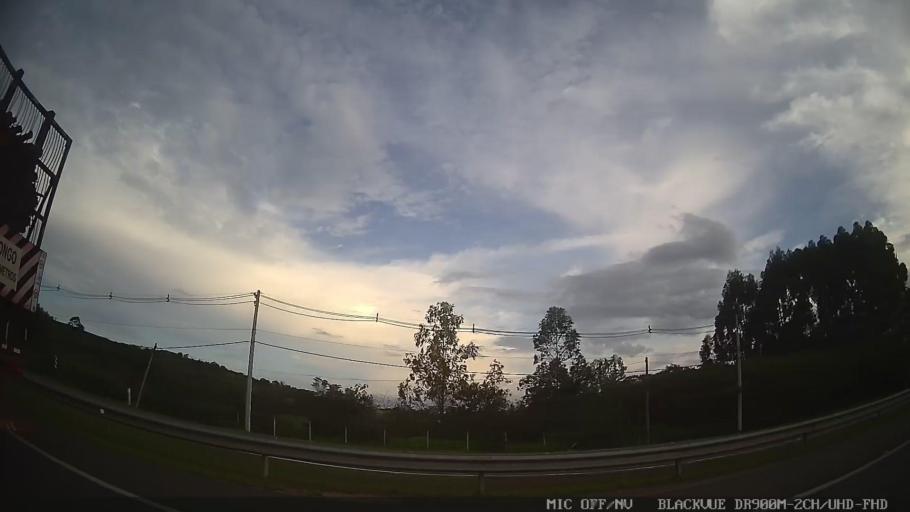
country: BR
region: Sao Paulo
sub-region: Porto Feliz
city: Porto Feliz
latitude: -23.2264
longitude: -47.5590
